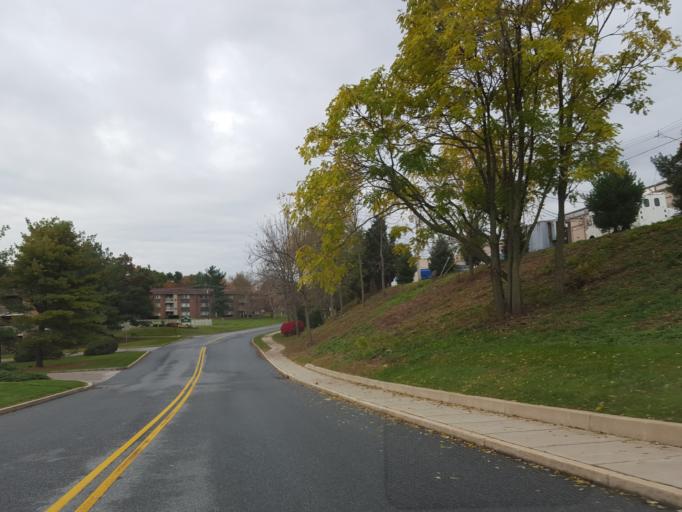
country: US
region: Pennsylvania
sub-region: York County
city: Valley View
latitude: 39.9414
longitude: -76.6910
